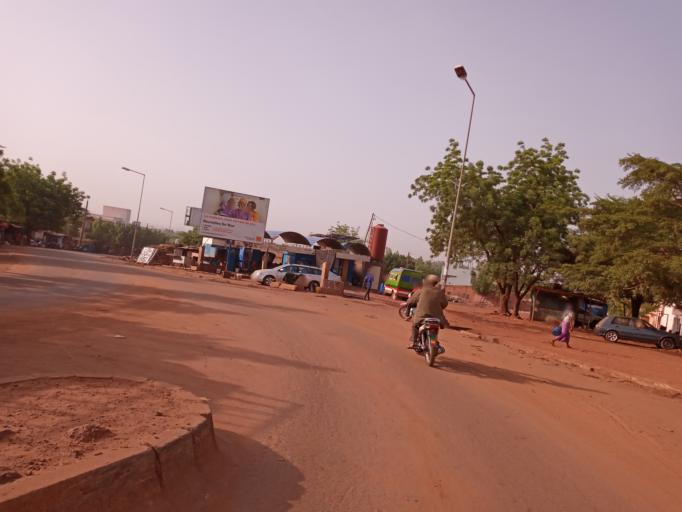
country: ML
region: Bamako
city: Bamako
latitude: 12.6629
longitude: -7.9791
